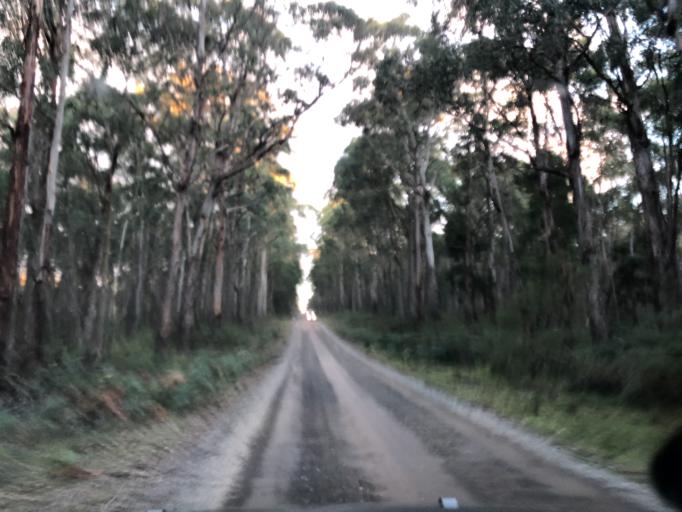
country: AU
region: Victoria
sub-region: Moorabool
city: Bacchus Marsh
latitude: -37.4196
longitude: 144.3979
